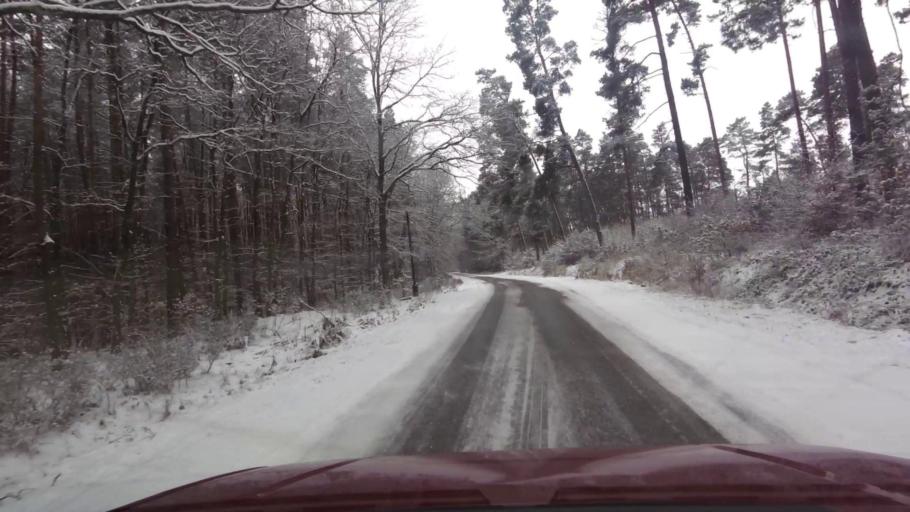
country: PL
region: West Pomeranian Voivodeship
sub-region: Powiat swidwinski
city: Rabino
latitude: 53.8937
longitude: 15.9399
